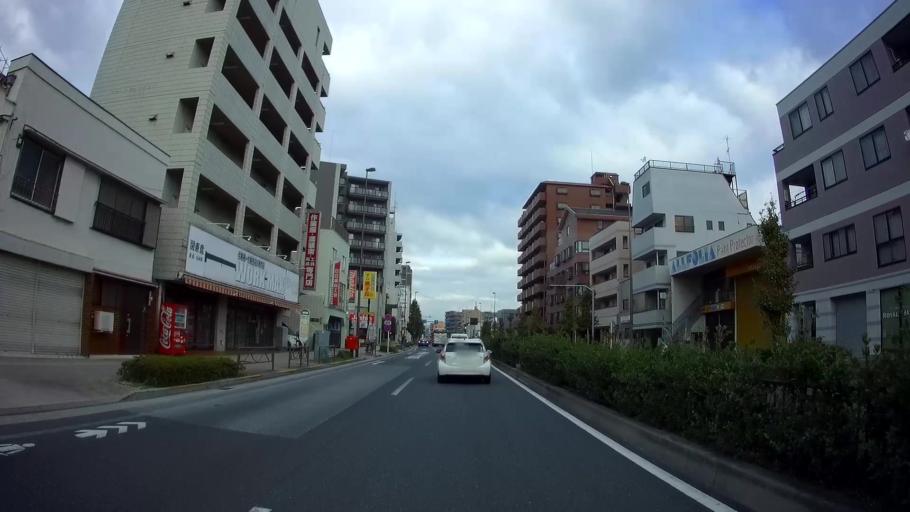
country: JP
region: Saitama
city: Shimotoda
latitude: 35.7579
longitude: 139.6833
